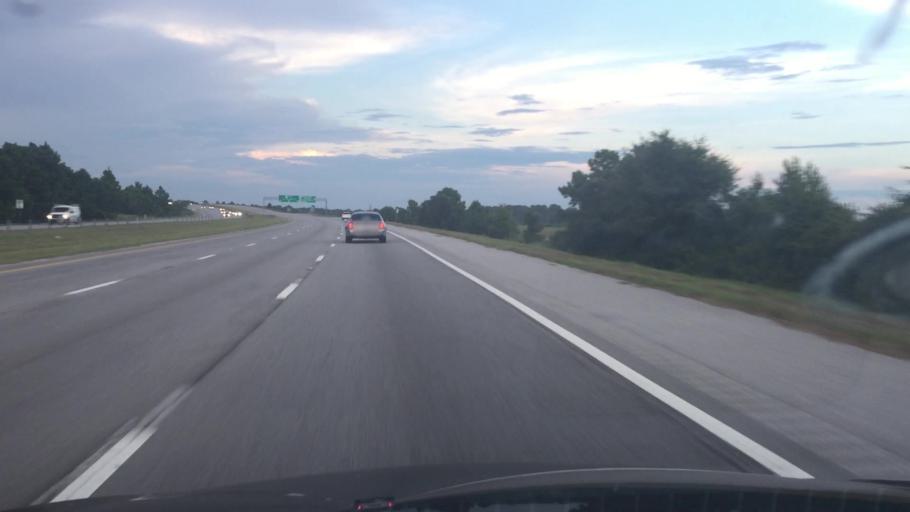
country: US
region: South Carolina
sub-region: Horry County
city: North Myrtle Beach
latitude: 33.8375
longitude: -78.7071
